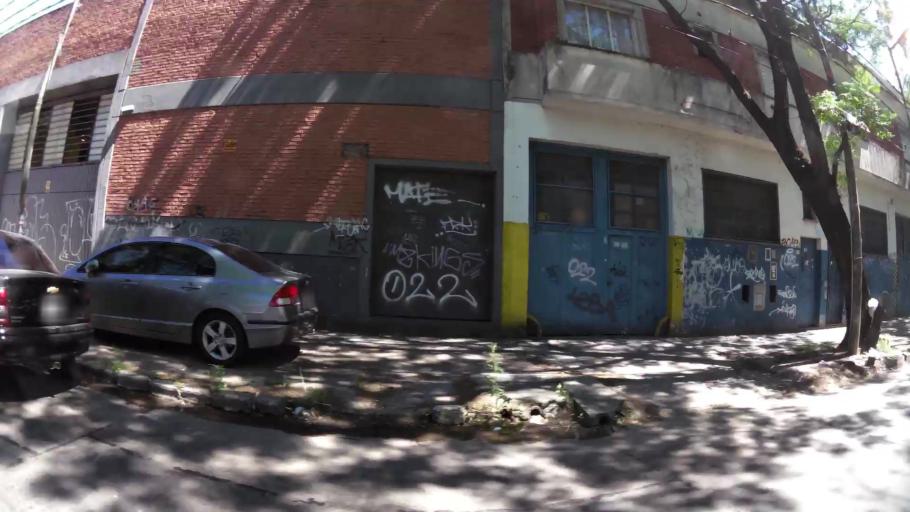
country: AR
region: Buenos Aires
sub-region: Partido de General San Martin
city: General San Martin
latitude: -34.5867
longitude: -58.5250
